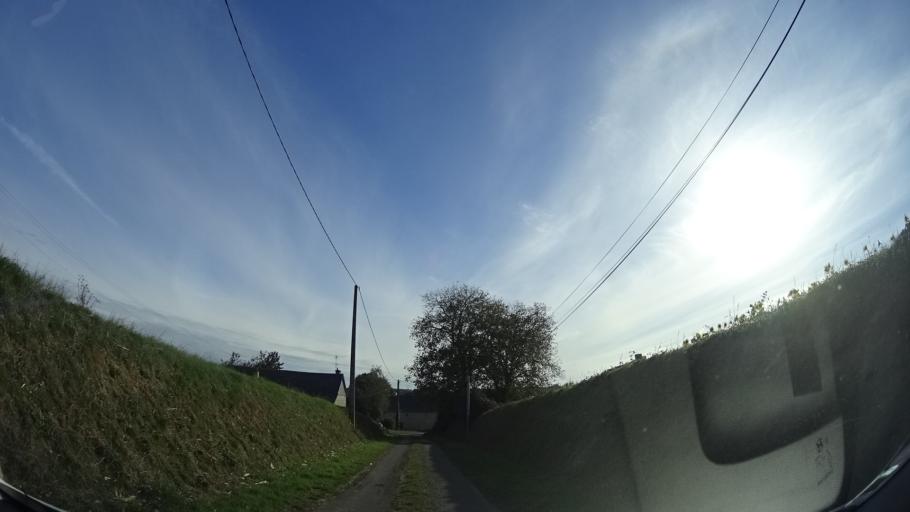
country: FR
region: Brittany
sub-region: Departement d'Ille-et-Vilaine
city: Geveze
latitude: 48.2196
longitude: -1.8083
